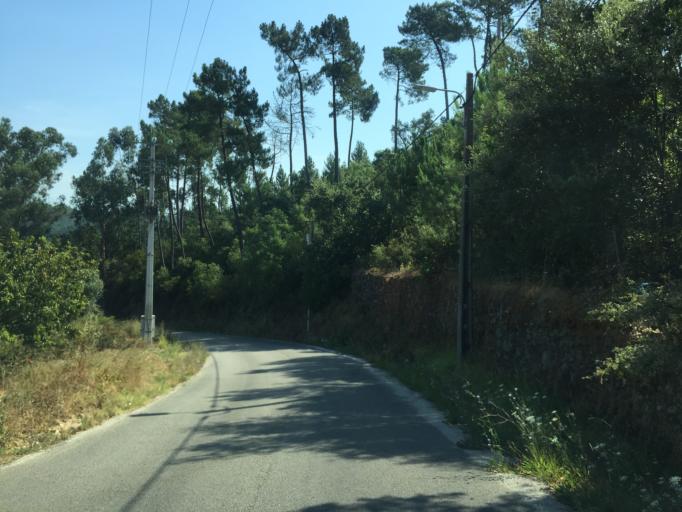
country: PT
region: Santarem
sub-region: Ferreira do Zezere
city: Ferreira do Zezere
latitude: 39.6074
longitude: -8.2825
